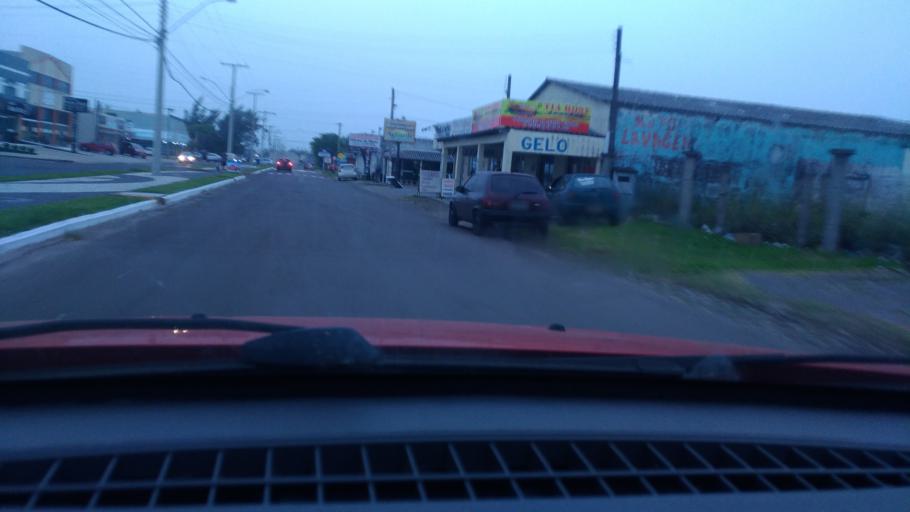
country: BR
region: Rio Grande do Sul
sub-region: Capao Da Canoa
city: Capao da Canoa
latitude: -29.8514
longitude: -50.0705
